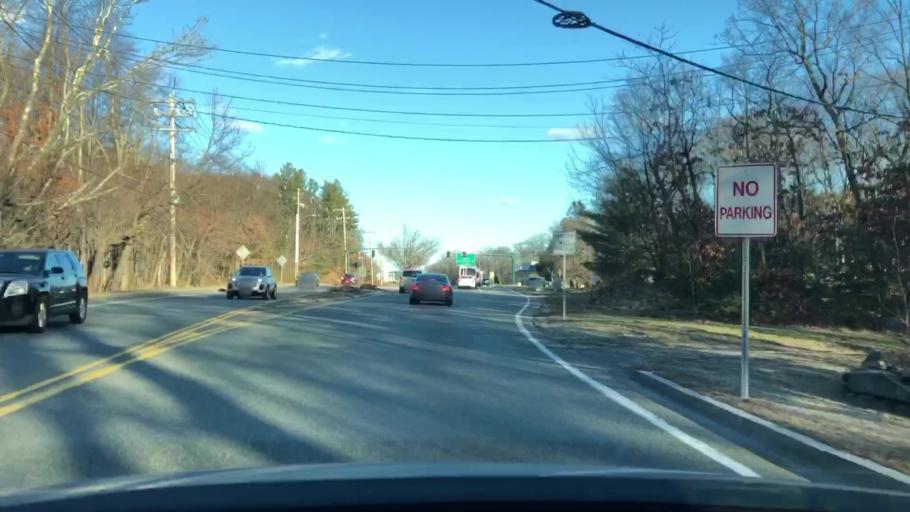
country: US
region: Massachusetts
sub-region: Norfolk County
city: Westwood
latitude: 42.2406
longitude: -71.2127
